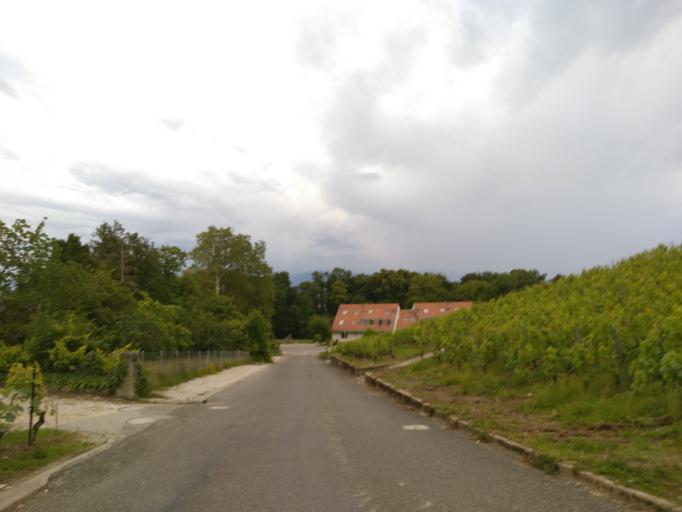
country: CH
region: Vaud
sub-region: Nyon District
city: Perroy
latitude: 46.4796
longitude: 6.3697
